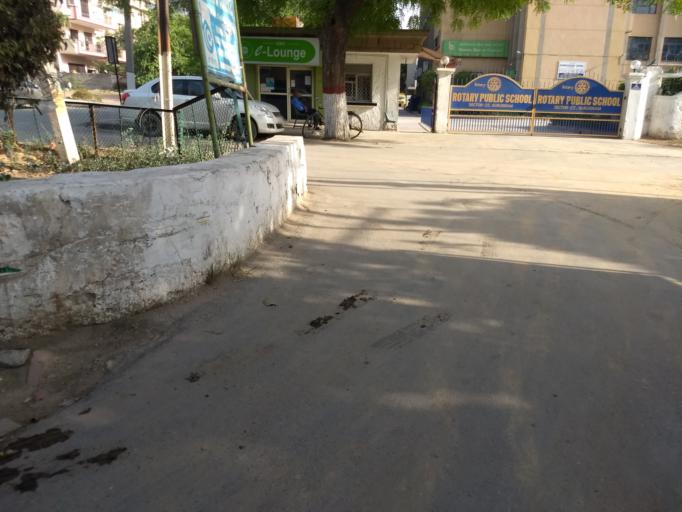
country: IN
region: Haryana
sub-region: Gurgaon
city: Gurgaon
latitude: 28.5026
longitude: 77.0631
